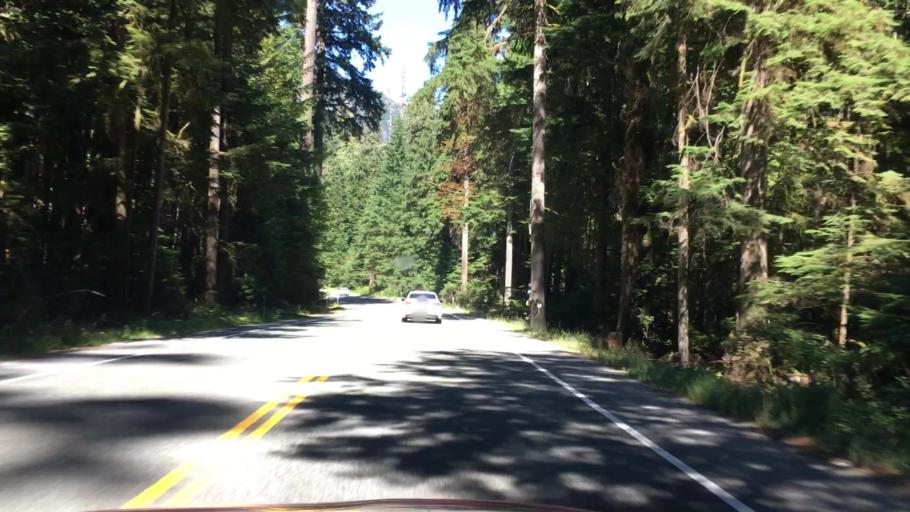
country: CA
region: British Columbia
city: Port Alberni
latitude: 49.2840
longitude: -124.6735
